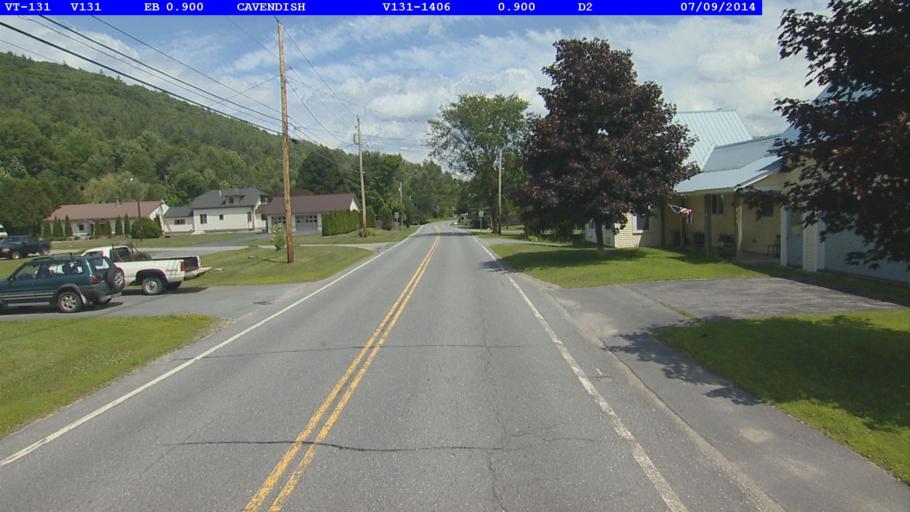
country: US
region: Vermont
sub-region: Windsor County
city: Chester
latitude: 43.3851
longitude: -72.6308
